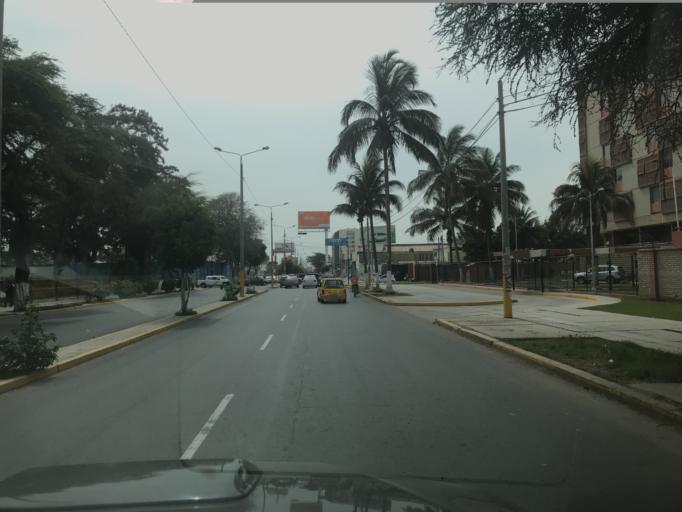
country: PE
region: Lambayeque
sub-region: Provincia de Chiclayo
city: Chiclayo
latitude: -6.7709
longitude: -79.8481
